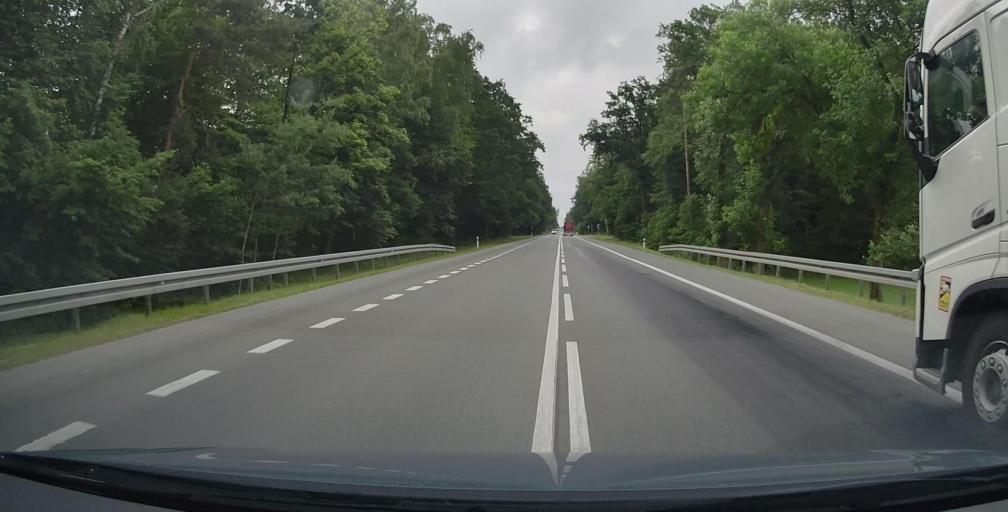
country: PL
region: Lublin Voivodeship
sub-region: Powiat lukowski
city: Trzebieszow
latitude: 52.0577
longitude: 22.6261
